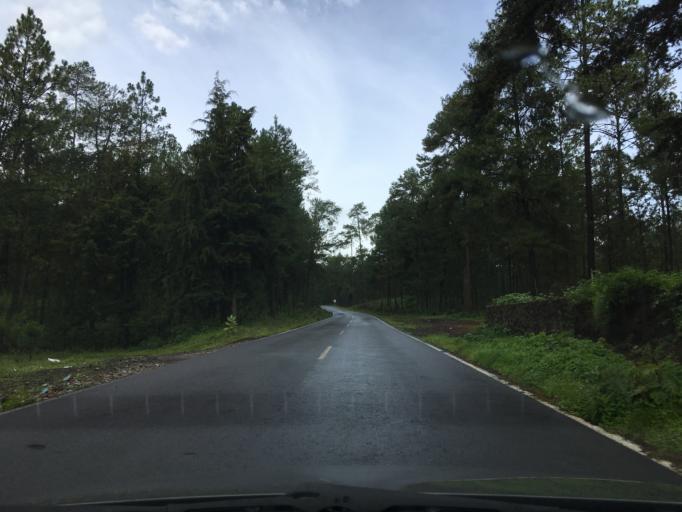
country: MX
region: Michoacan
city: Nuevo San Juan Parangaricutiro
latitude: 19.4435
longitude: -102.1586
